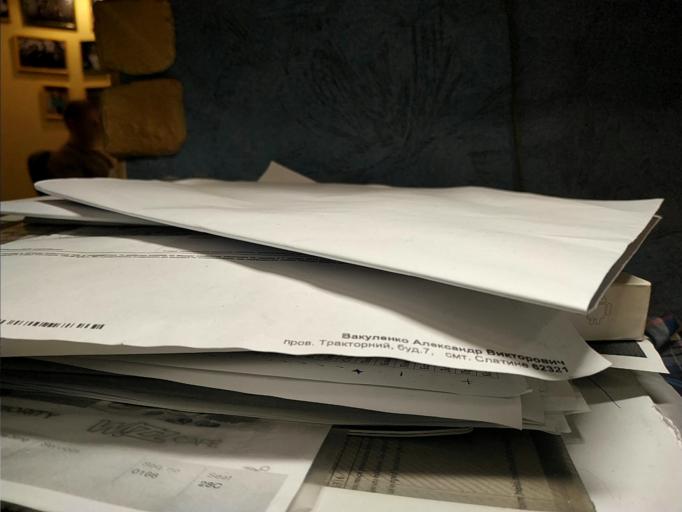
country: RU
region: Tverskaya
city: Zubtsov
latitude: 56.1086
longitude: 34.6396
